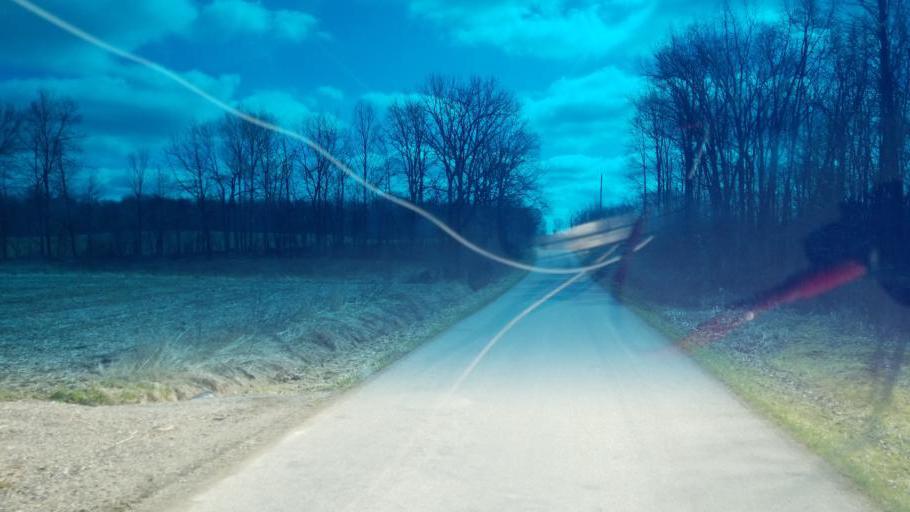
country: US
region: Ohio
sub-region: Richland County
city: Lexington
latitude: 40.6641
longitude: -82.6956
